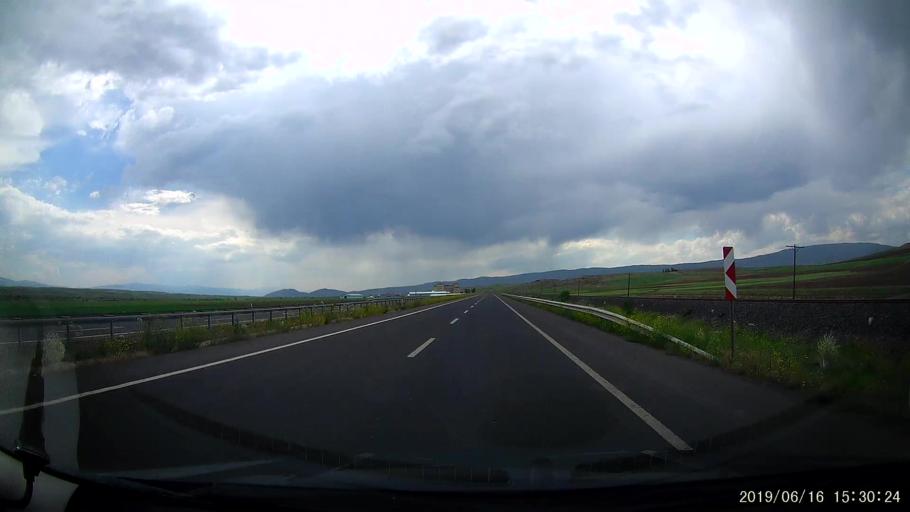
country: TR
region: Erzurum
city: Horasan
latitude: 40.0337
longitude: 42.1063
